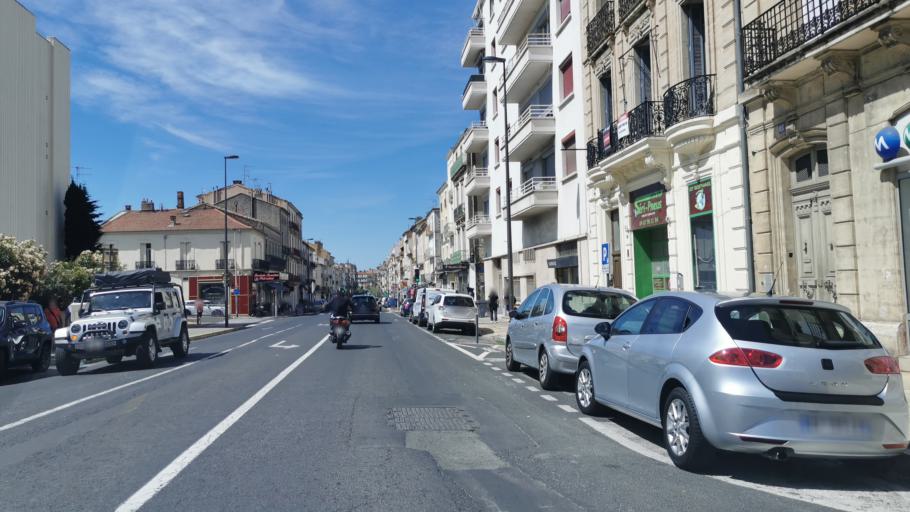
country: FR
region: Languedoc-Roussillon
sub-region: Departement de l'Herault
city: Beziers
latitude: 43.3493
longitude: 3.2212
